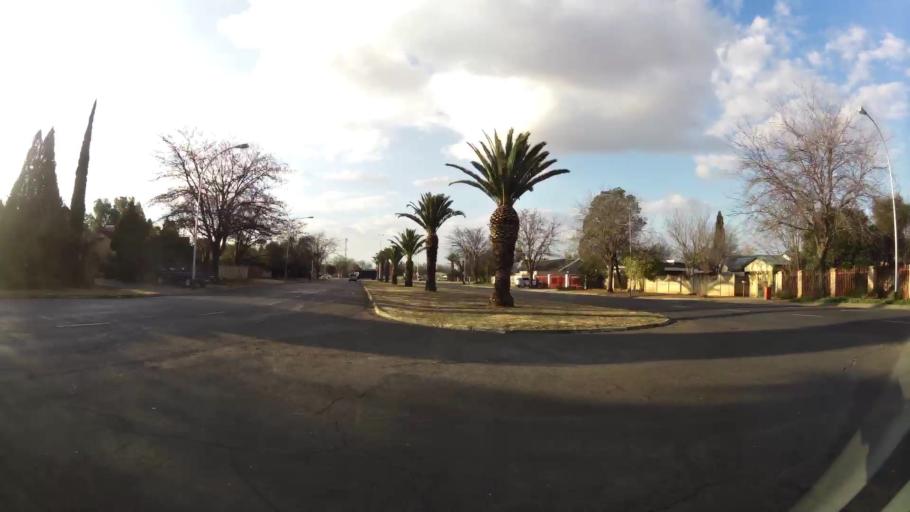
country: ZA
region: Orange Free State
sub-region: Mangaung Metropolitan Municipality
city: Bloemfontein
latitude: -29.1462
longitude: 26.1886
